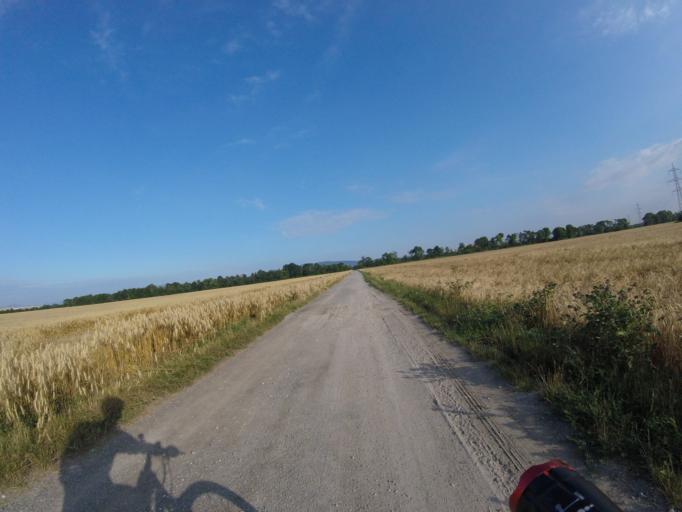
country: AT
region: Lower Austria
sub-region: Politischer Bezirk Baden
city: Trumau
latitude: 47.9999
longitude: 16.3719
